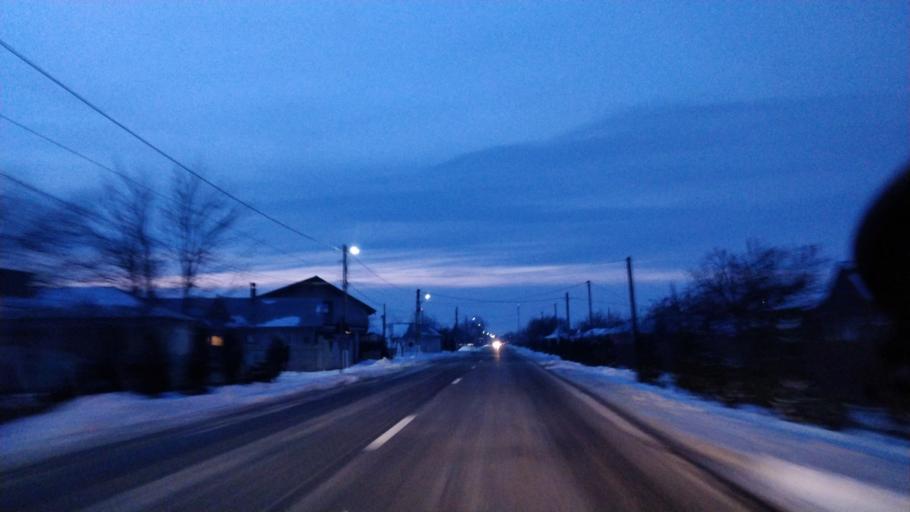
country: RO
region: Vrancea
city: Vulturu de Sus
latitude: 45.6151
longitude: 27.4310
